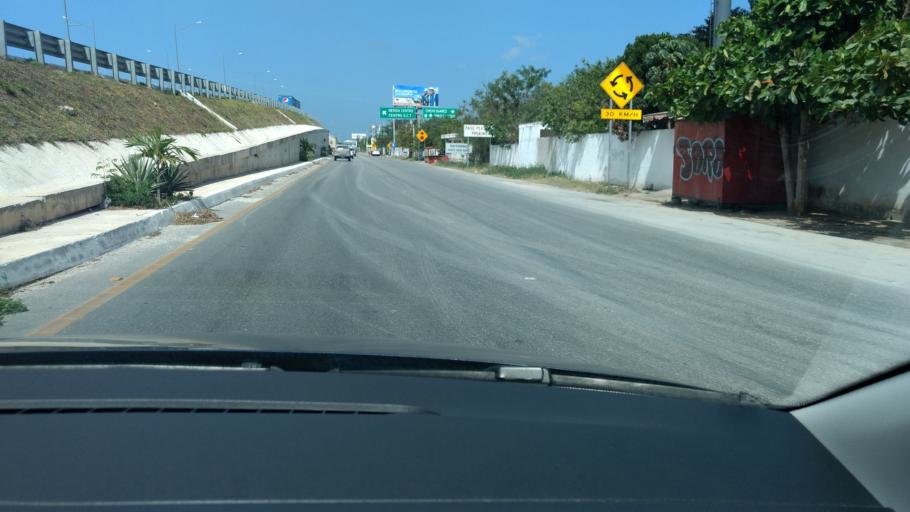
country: MX
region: Yucatan
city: Merida
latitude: 20.9970
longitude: -89.5614
